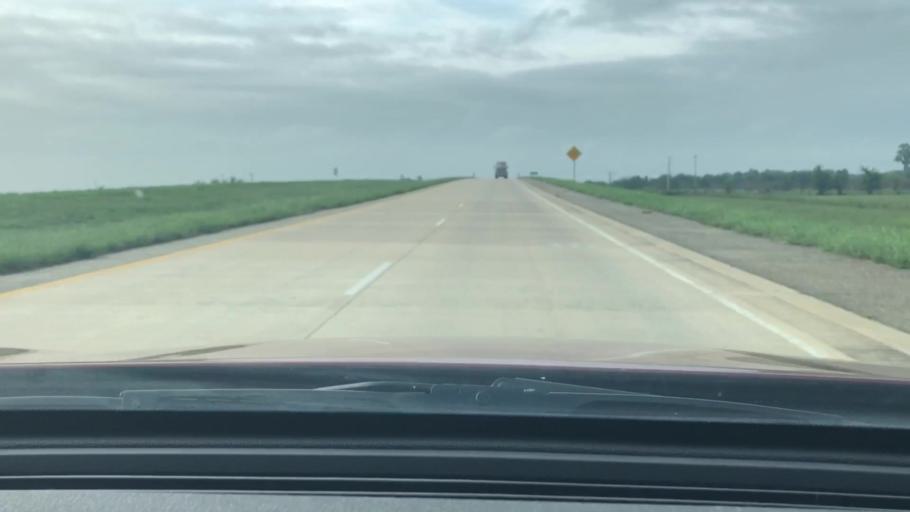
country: US
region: Louisiana
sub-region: Caddo Parish
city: Vivian
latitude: 32.8831
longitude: -93.8604
